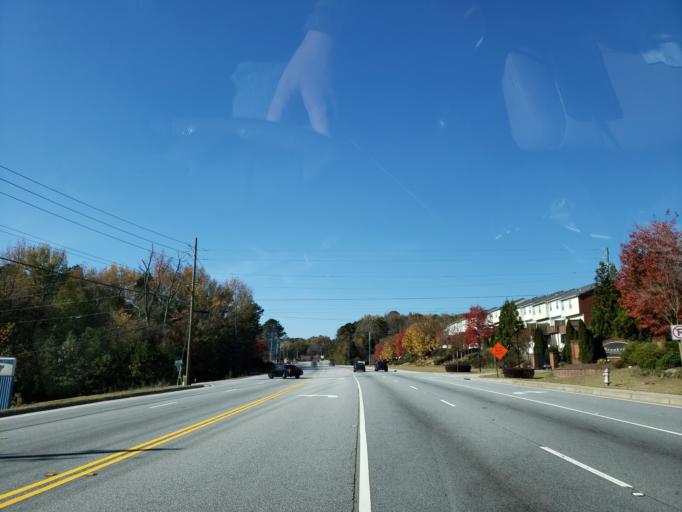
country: US
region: Georgia
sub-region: Cobb County
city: Mableton
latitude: 33.7856
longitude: -84.5435
